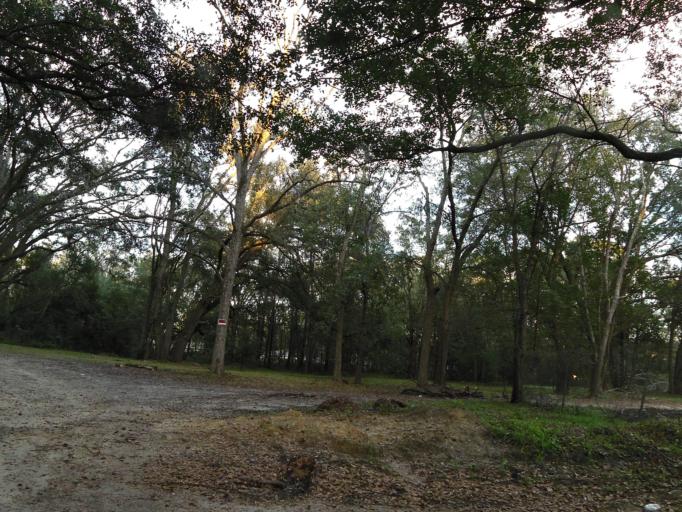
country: US
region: Florida
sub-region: Duval County
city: Jacksonville
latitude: 30.2796
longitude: -81.6401
